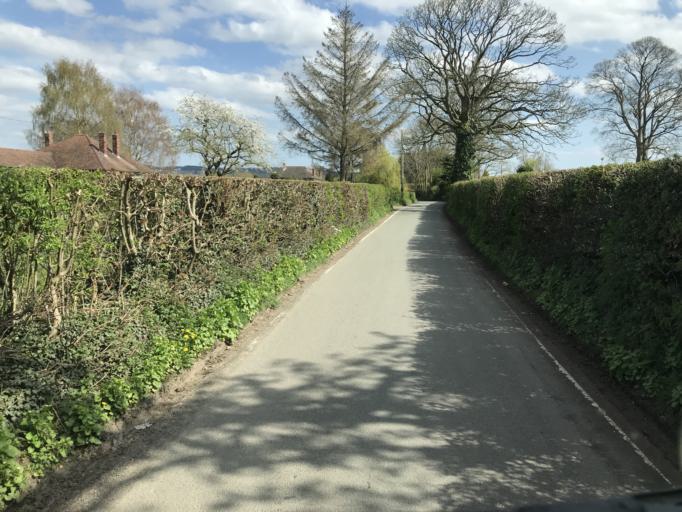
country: GB
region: England
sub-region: Cheshire West and Chester
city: Tarvin
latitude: 53.2039
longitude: -2.7595
